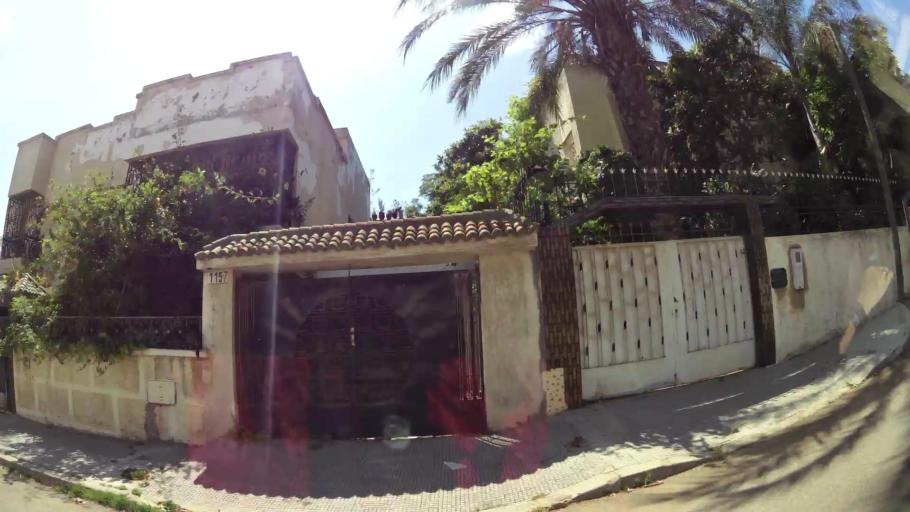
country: MA
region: Rabat-Sale-Zemmour-Zaer
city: Sale
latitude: 34.0434
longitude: -6.7856
